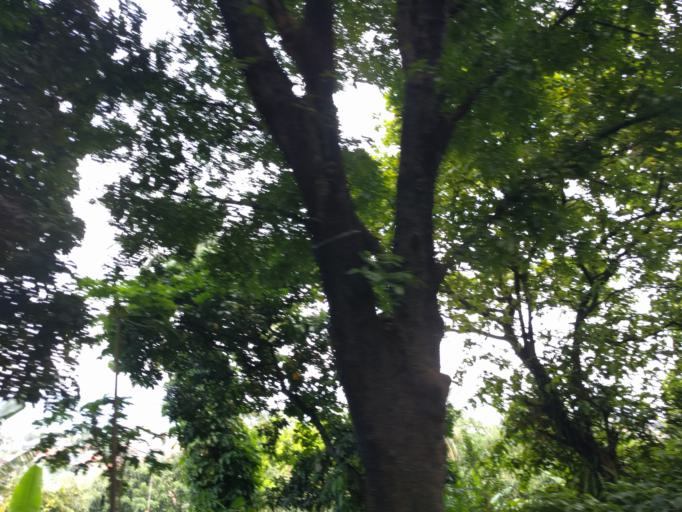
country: ID
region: West Java
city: Bogor
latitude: -6.6098
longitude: 106.8110
